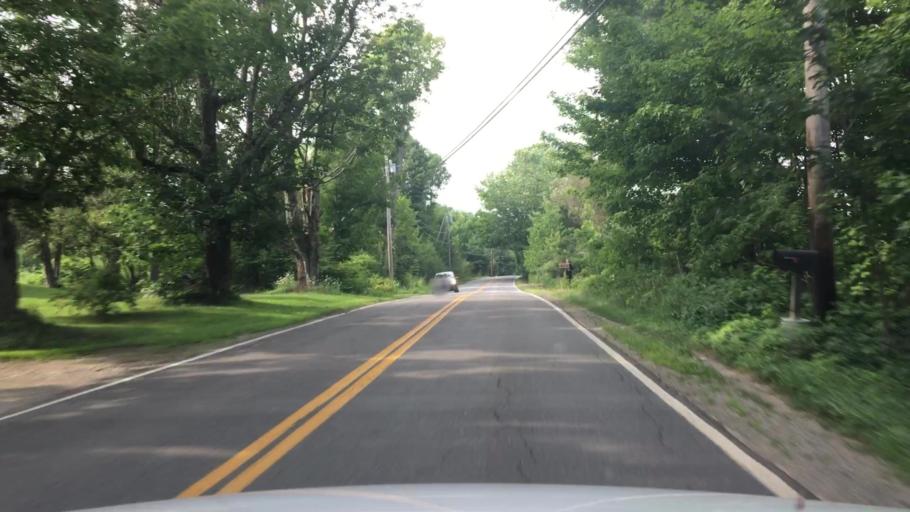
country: US
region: Maine
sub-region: Lincoln County
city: Waldoboro
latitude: 44.1488
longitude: -69.3741
